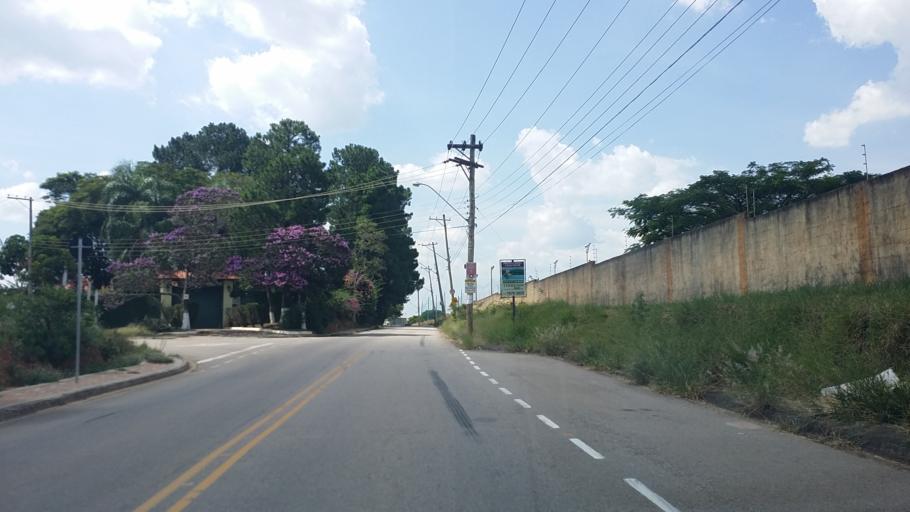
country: BR
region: Sao Paulo
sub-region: Itupeva
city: Itupeva
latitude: -23.2092
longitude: -47.0185
